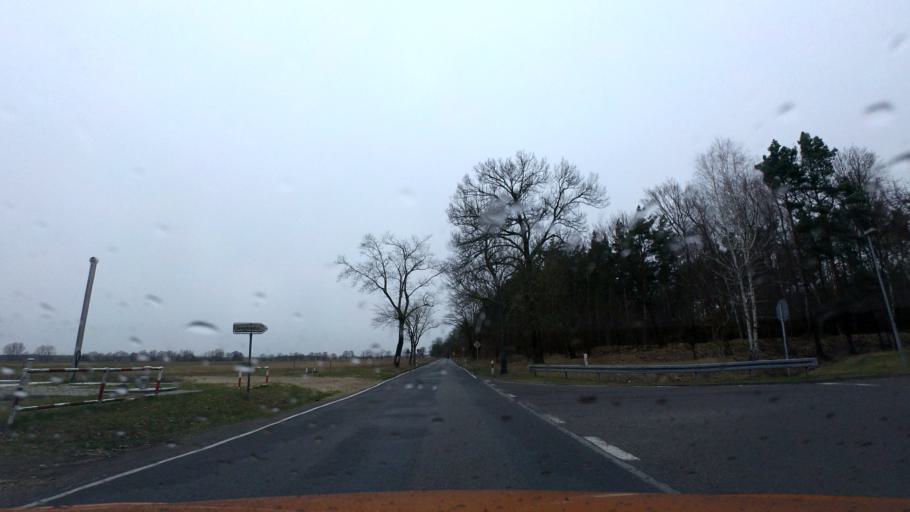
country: DE
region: Brandenburg
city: Falkensee
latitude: 52.6310
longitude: 13.0756
